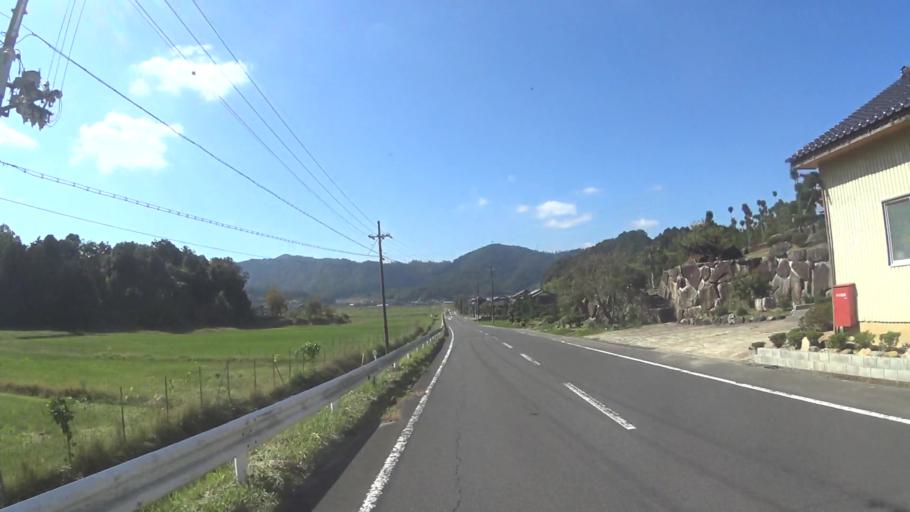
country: JP
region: Hyogo
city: Toyooka
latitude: 35.5820
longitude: 134.9411
